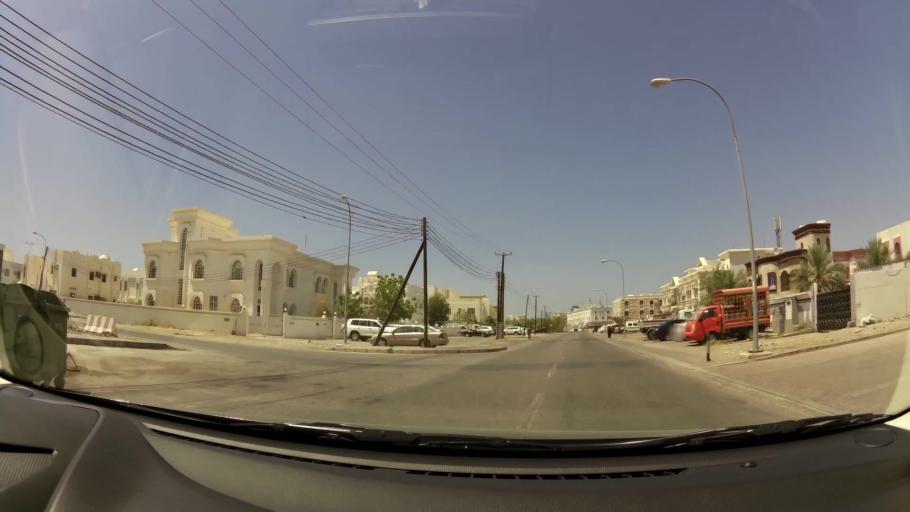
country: OM
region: Muhafazat Masqat
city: Bawshar
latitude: 23.5932
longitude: 58.3781
